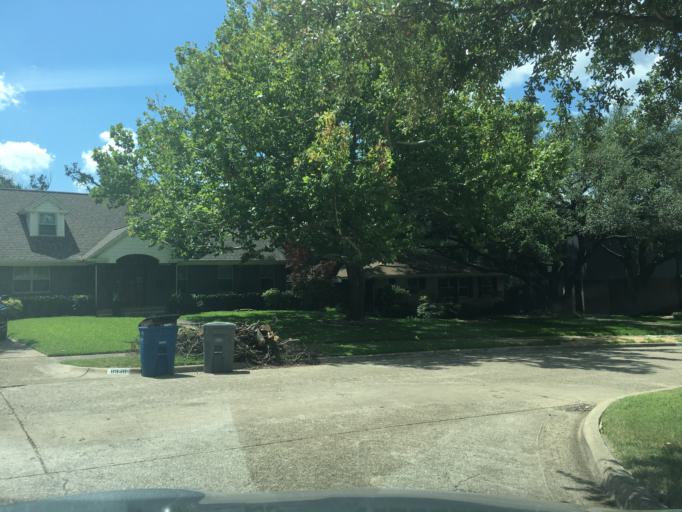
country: US
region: Texas
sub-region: Dallas County
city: Richardson
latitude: 32.8707
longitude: -96.7120
